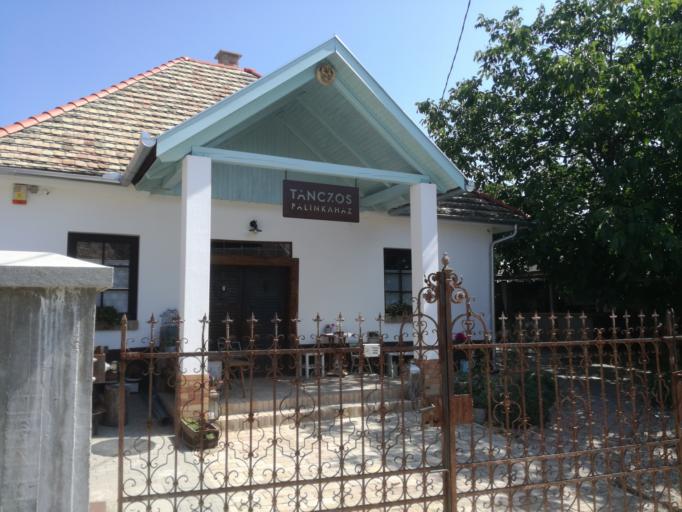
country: HU
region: Baranya
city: Lanycsok
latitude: 46.0252
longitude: 18.6560
